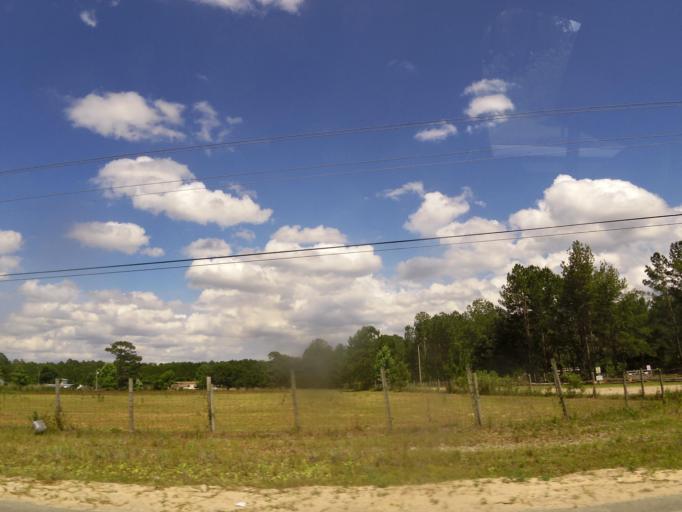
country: US
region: Florida
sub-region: Clay County
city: Keystone Heights
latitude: 29.8510
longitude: -81.9178
